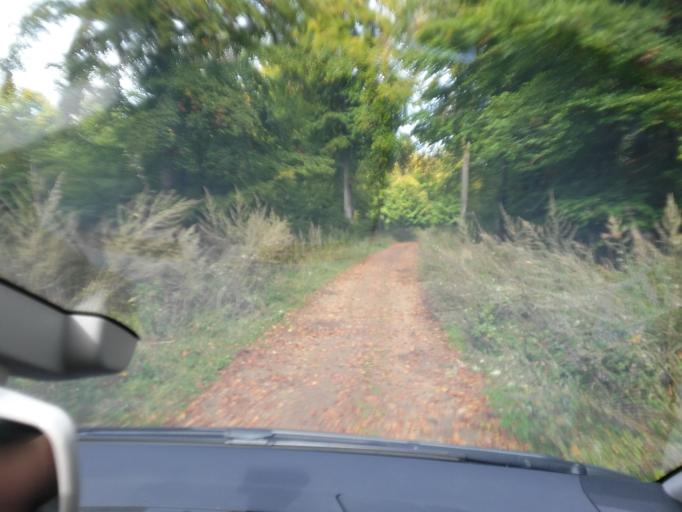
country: BE
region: Wallonia
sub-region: Province du Luxembourg
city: Attert
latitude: 49.7143
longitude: 5.7663
